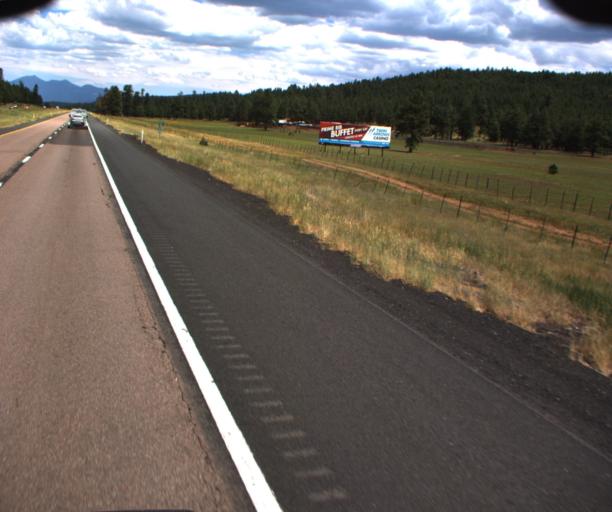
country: US
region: Arizona
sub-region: Coconino County
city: Mountainaire
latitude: 35.0069
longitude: -111.6855
